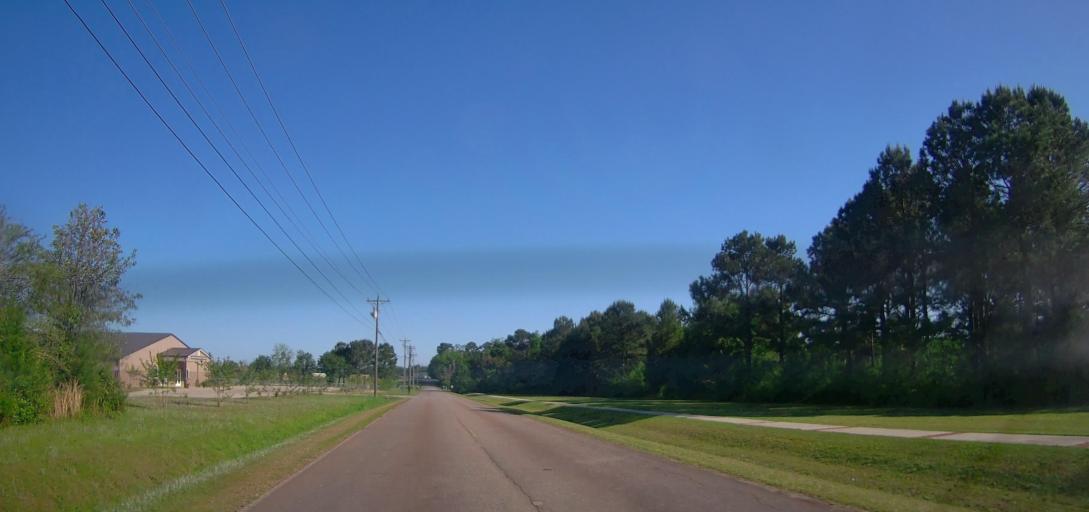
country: US
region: Georgia
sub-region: Houston County
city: Perry
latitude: 32.4705
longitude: -83.7068
